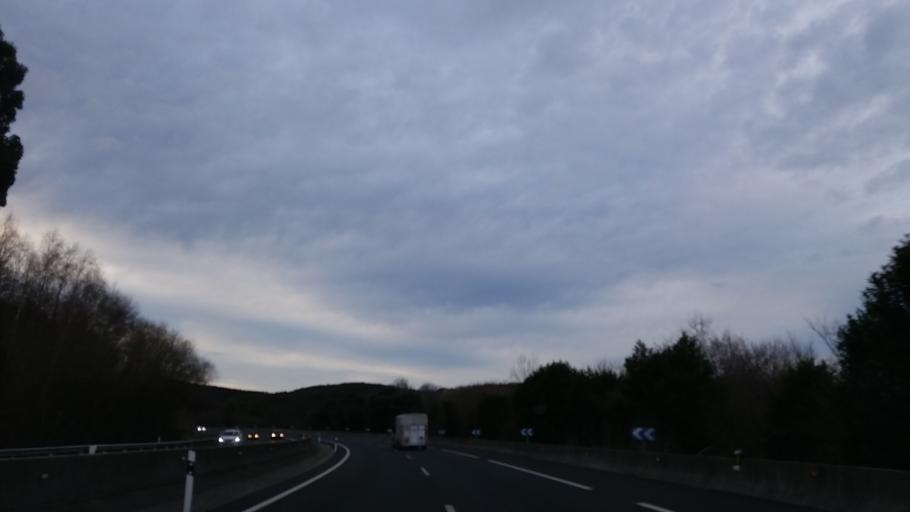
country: ES
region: Cantabria
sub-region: Provincia de Cantabria
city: Liendo
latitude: 43.3863
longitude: -3.3851
